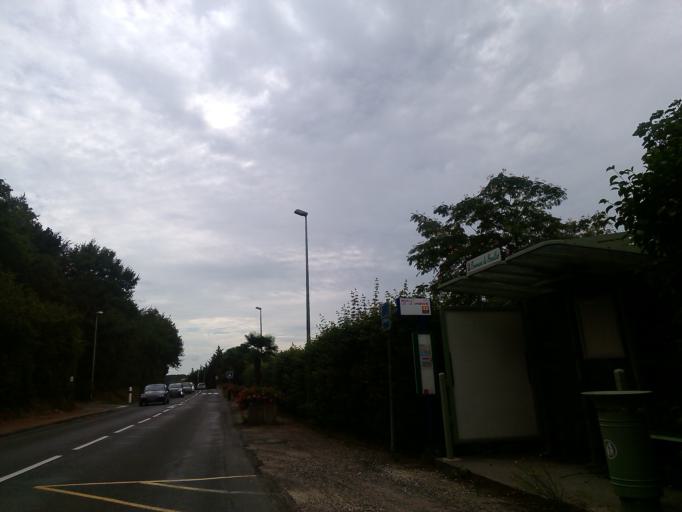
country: FR
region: Poitou-Charentes
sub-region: Departement de la Charente-Maritime
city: Breuillet
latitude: 45.6884
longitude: -1.0569
